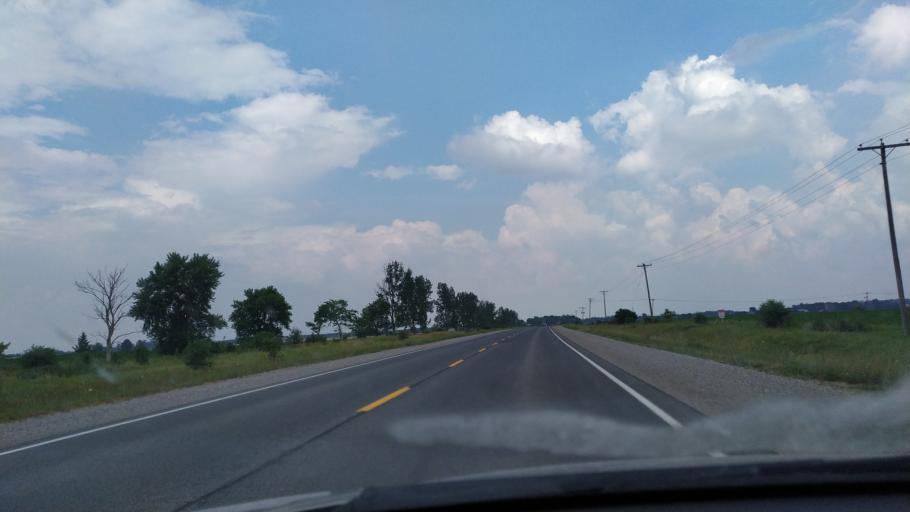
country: CA
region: Ontario
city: Stratford
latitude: 43.2405
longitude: -81.1031
